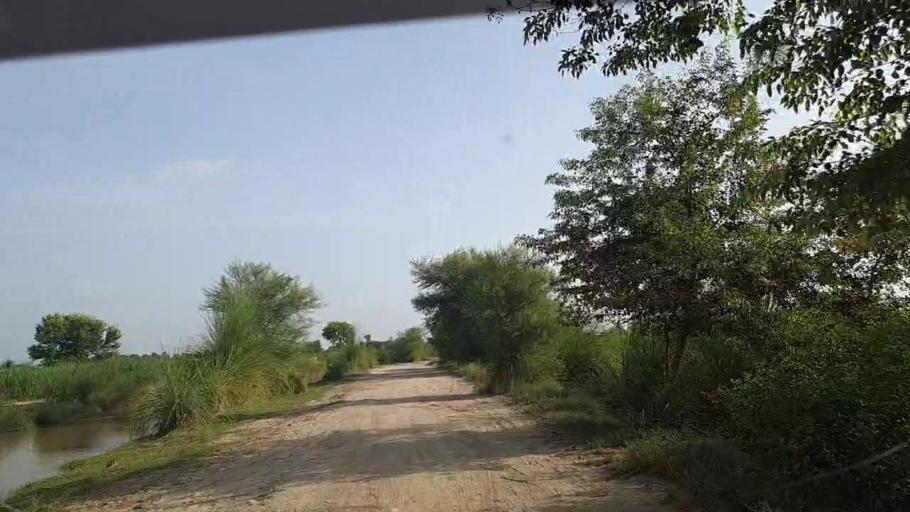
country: PK
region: Sindh
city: Ghotki
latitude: 27.9980
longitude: 69.2617
